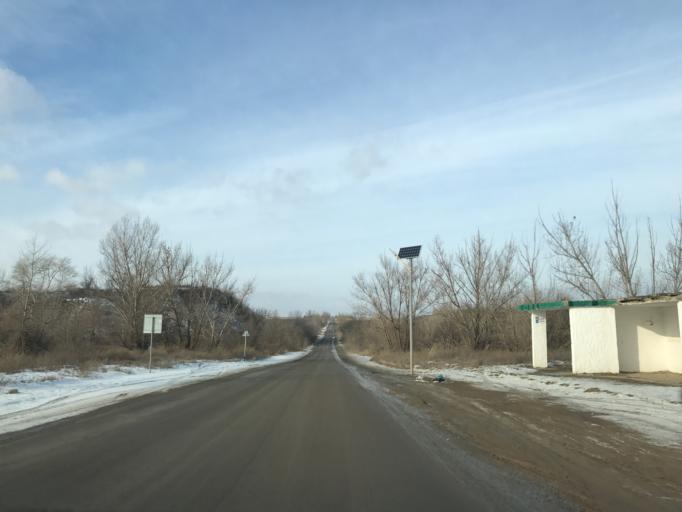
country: RU
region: Rostov
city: Staraya Stanitsa
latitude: 48.2382
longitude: 40.4044
